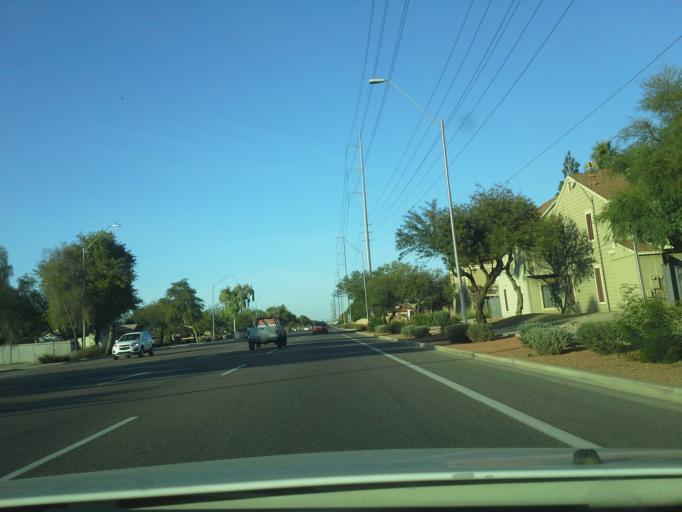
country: US
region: Arizona
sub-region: Maricopa County
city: Peoria
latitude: 33.6567
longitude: -112.1344
